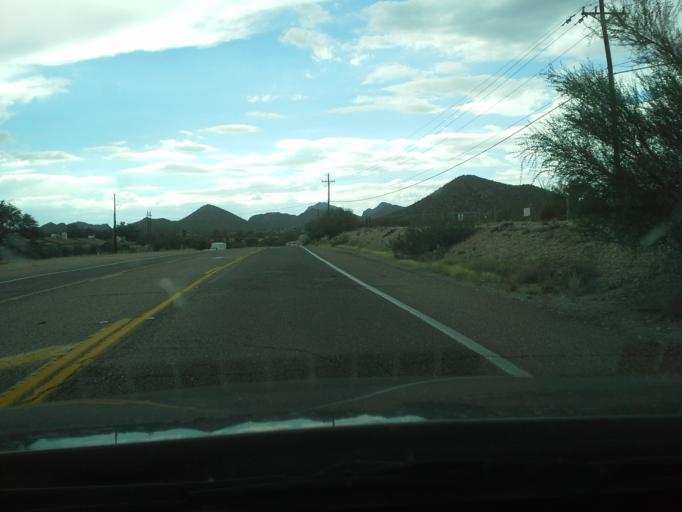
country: US
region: Arizona
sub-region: Pima County
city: South Tucson
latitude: 32.2069
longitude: -111.0126
